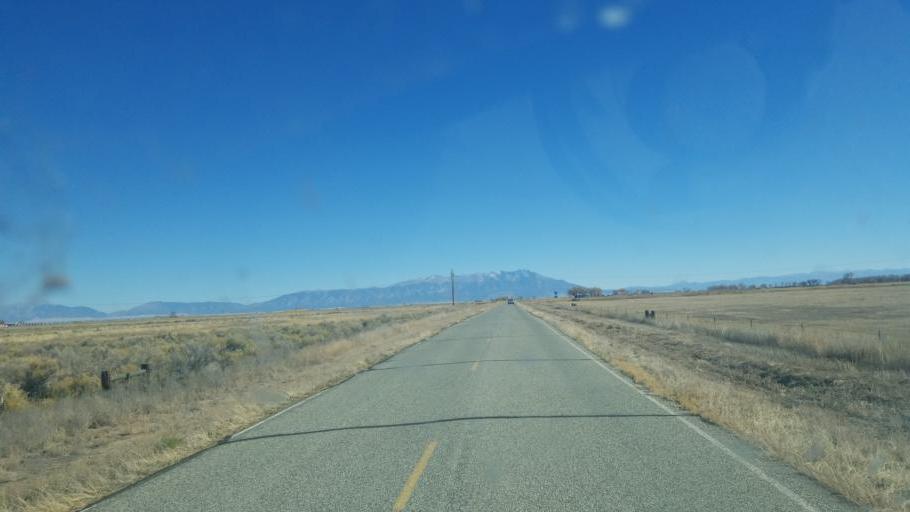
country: US
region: Colorado
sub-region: Rio Grande County
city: Monte Vista
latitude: 37.5743
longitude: -106.0063
